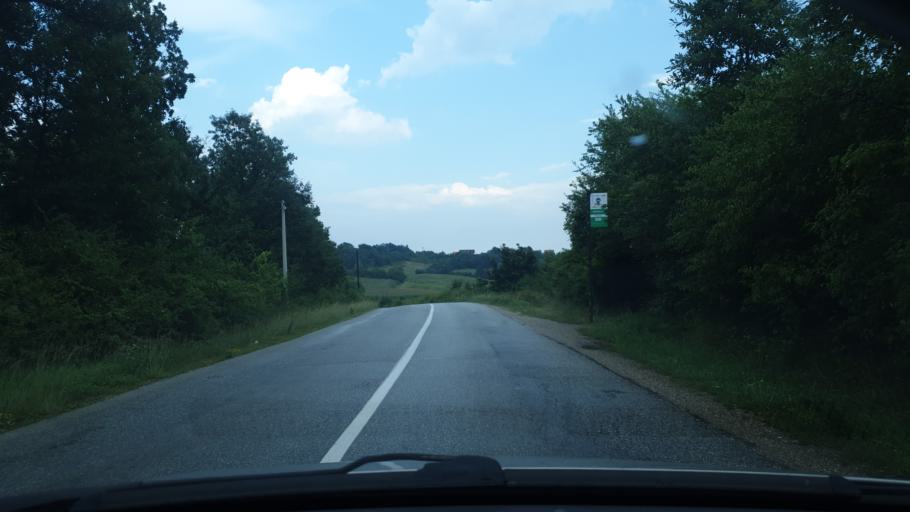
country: RS
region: Central Serbia
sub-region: Sumadijski Okrug
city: Kragujevac
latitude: 44.0457
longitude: 20.7875
